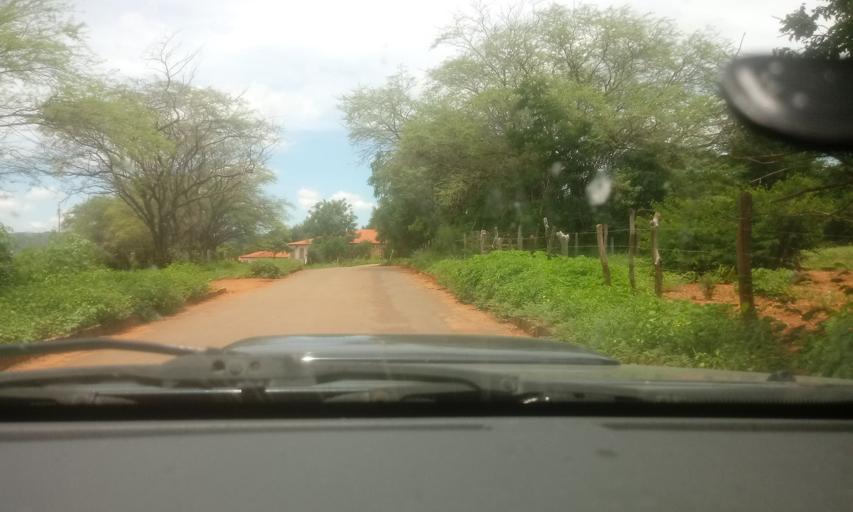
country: BR
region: Bahia
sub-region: Riacho De Santana
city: Riacho de Santana
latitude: -13.6005
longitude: -42.9450
